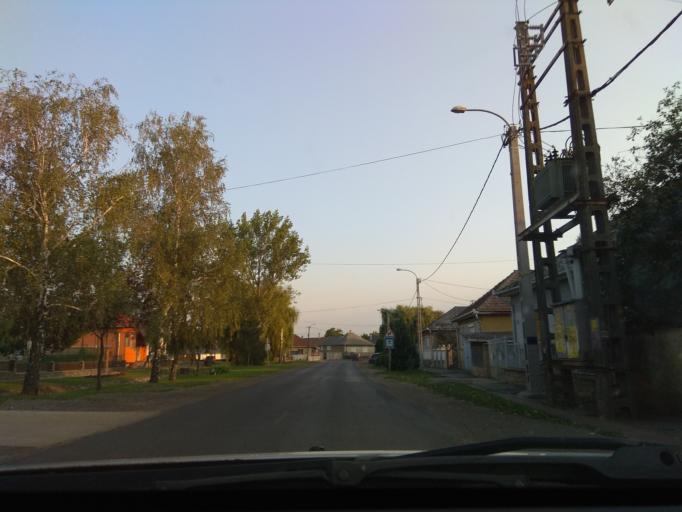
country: HU
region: Borsod-Abauj-Zemplen
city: Tallya
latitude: 48.2128
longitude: 21.2259
